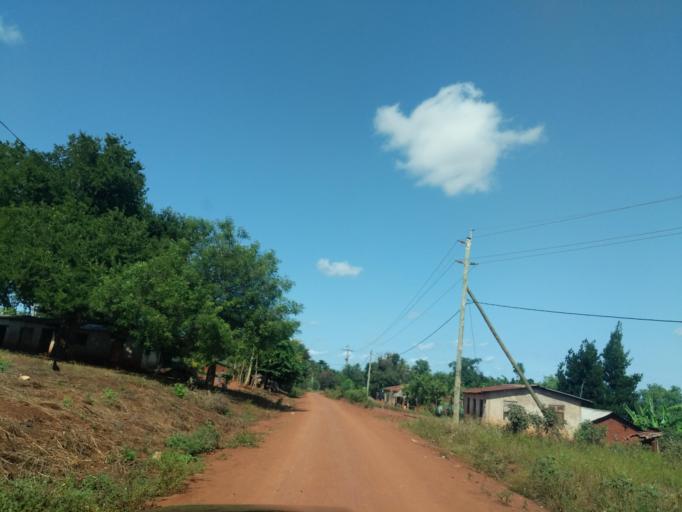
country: TZ
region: Tanga
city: Muheza
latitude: -5.3834
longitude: 38.5799
